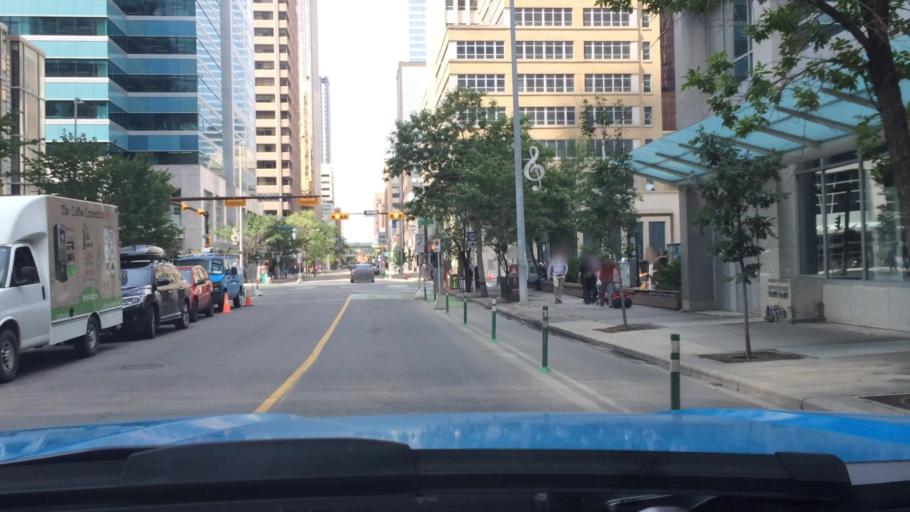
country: CA
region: Alberta
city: Calgary
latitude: 51.0459
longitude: -114.0730
